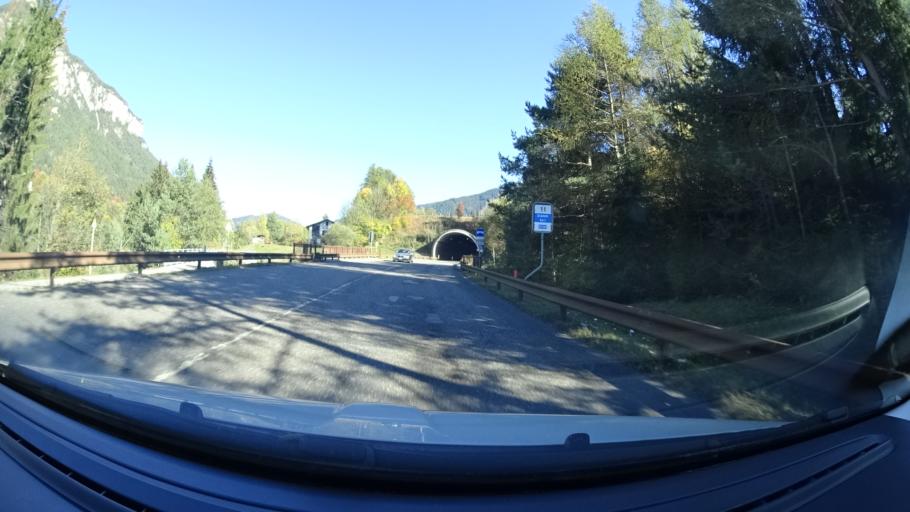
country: IT
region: Trentino-Alto Adige
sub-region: Provincia di Trento
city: Panchia
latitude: 46.2821
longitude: 11.5412
